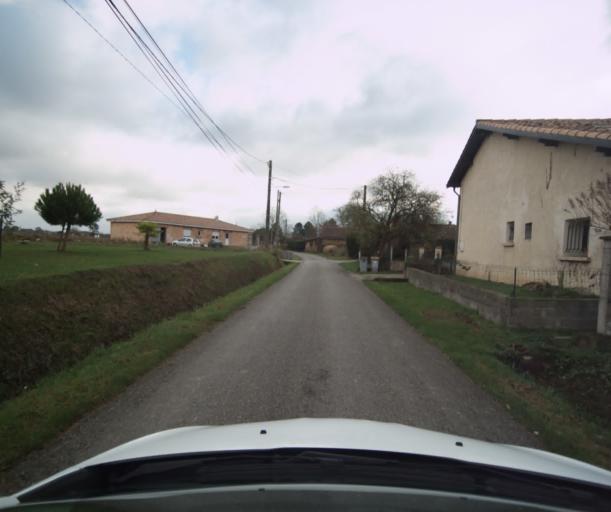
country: FR
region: Midi-Pyrenees
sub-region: Departement du Tarn-et-Garonne
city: Castelsarrasin
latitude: 44.0383
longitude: 1.1246
